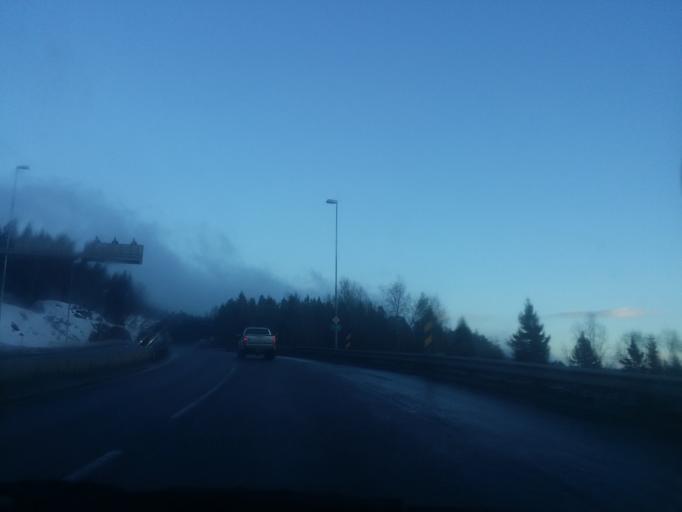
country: NO
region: Buskerud
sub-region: Hole
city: Vik
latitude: 59.9775
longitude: 10.3243
